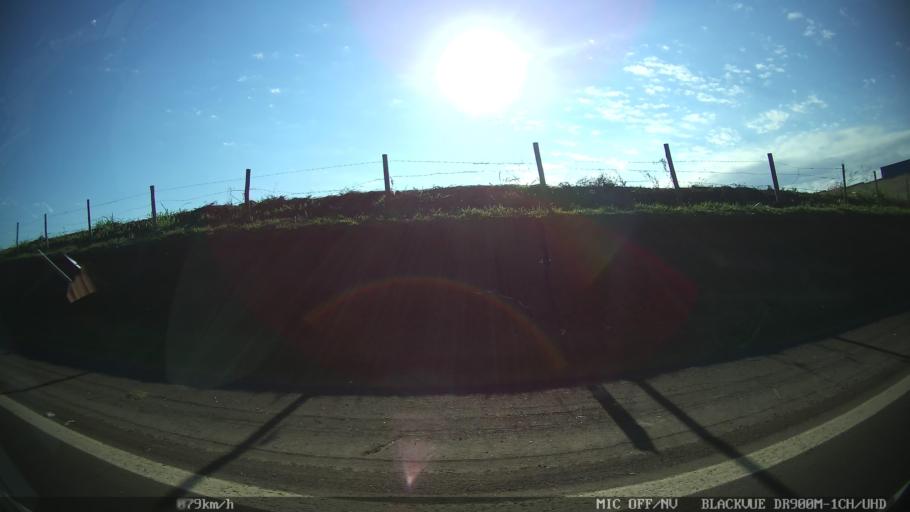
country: BR
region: Sao Paulo
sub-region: Piracicaba
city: Piracicaba
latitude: -22.6759
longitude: -47.6327
